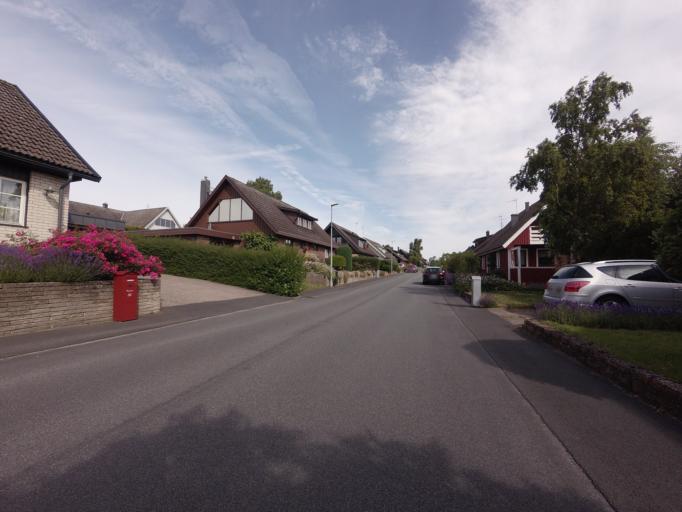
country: SE
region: Skane
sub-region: Simrishamns Kommun
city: Simrishamn
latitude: 55.5411
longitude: 14.3504
